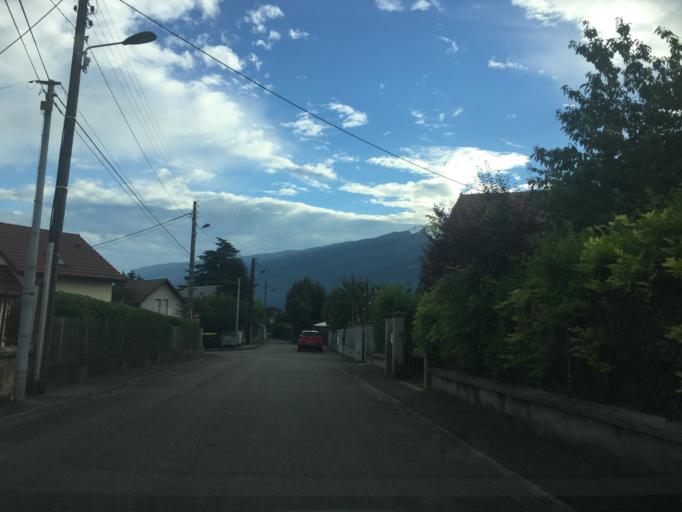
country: FR
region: Rhone-Alpes
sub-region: Departement de la Savoie
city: Brison-Saint-Innocent
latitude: 45.7035
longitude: 5.9060
